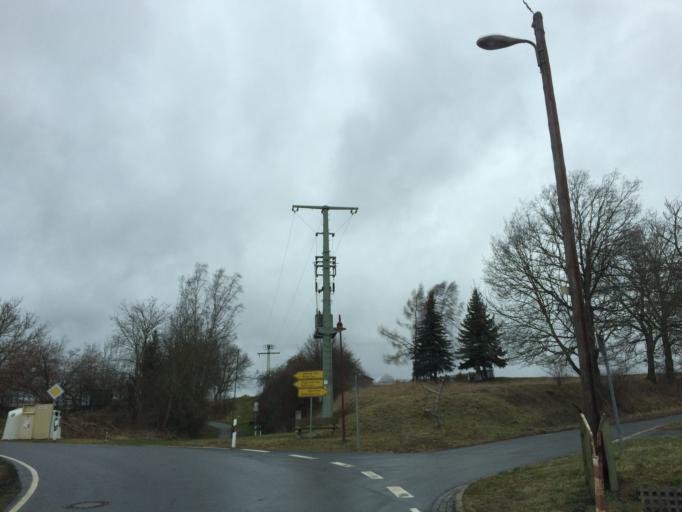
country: DE
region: Thuringia
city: Knau
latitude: 50.6554
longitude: 11.7155
